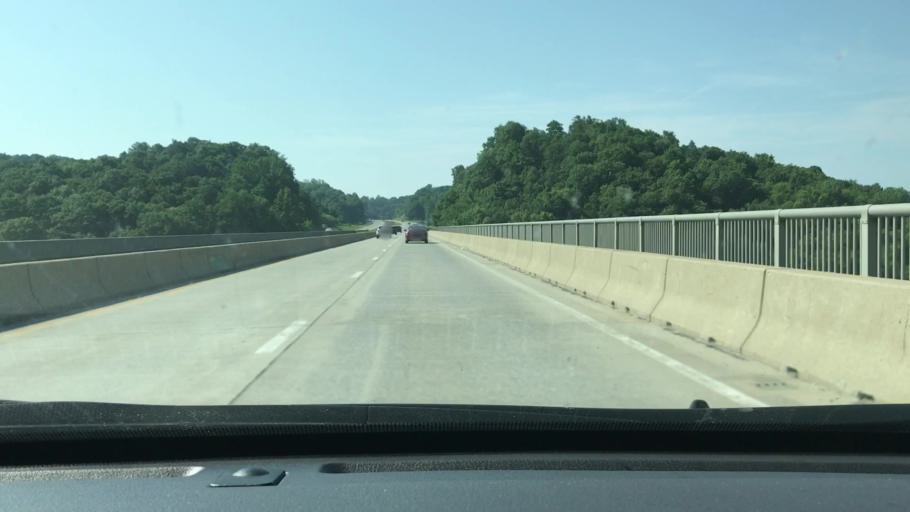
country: US
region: West Virginia
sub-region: Nicholas County
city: Summersville
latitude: 38.2411
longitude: -80.8548
